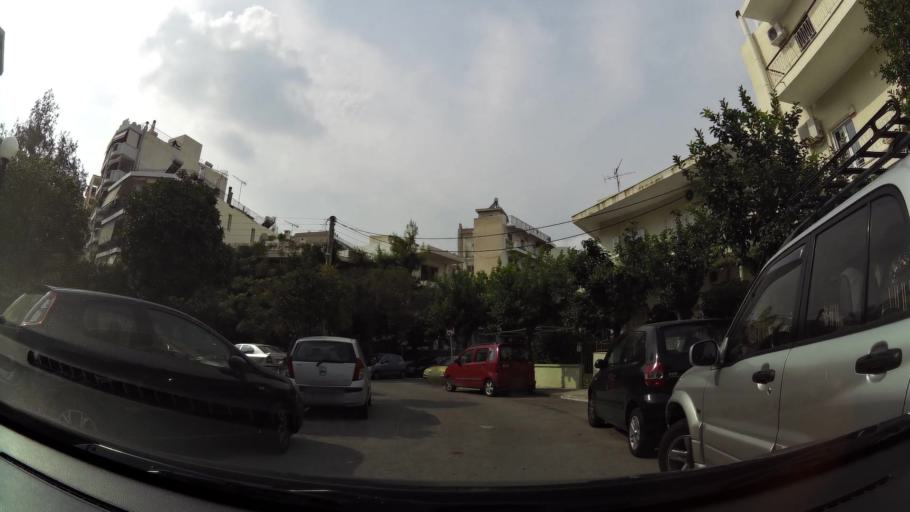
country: GR
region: Attica
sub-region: Nomarchia Athinas
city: Moskhaton
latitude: 37.9509
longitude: 23.6677
